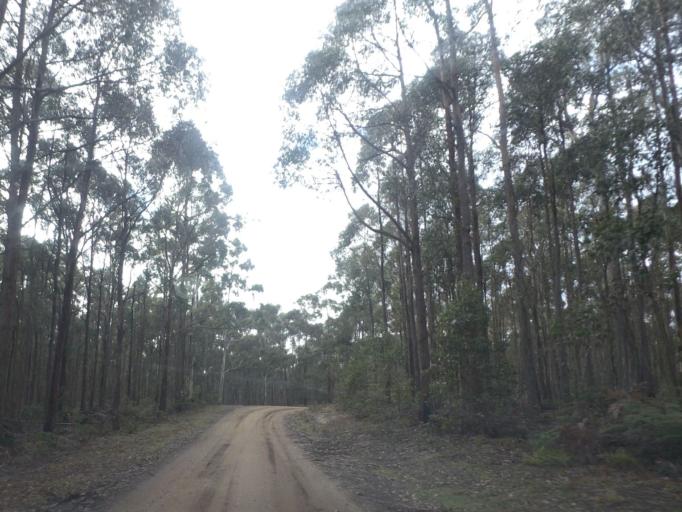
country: AU
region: Victoria
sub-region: Moorabool
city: Bacchus Marsh
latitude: -37.4221
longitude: 144.4057
